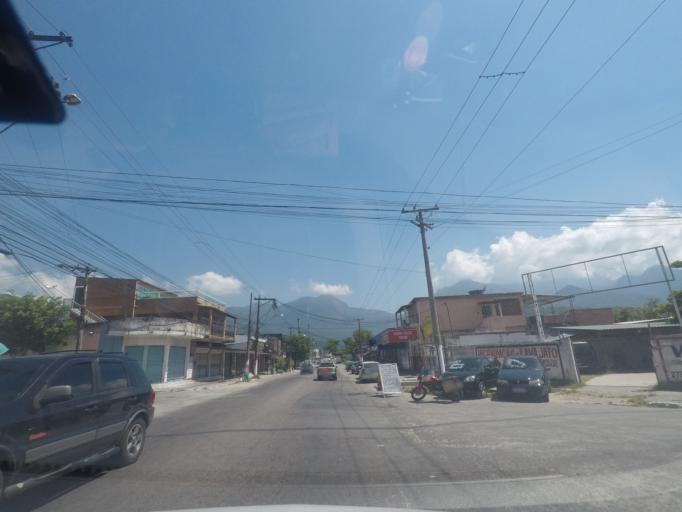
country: BR
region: Rio de Janeiro
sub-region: Petropolis
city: Petropolis
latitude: -22.5990
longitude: -43.1874
